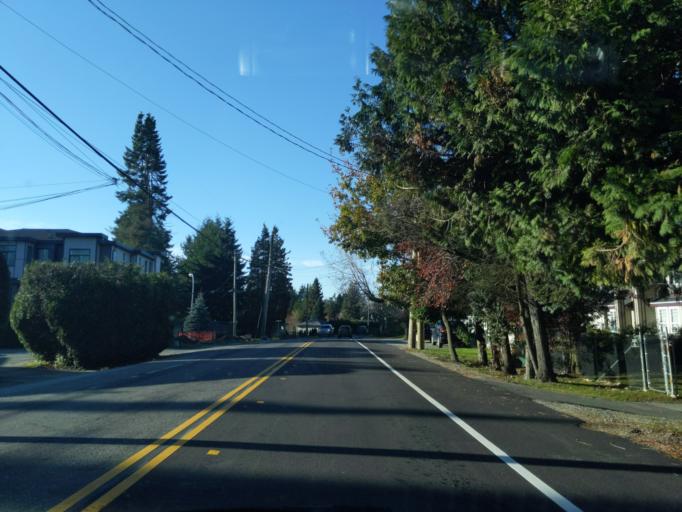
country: CA
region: British Columbia
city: New Westminster
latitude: 49.1888
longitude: -122.8601
